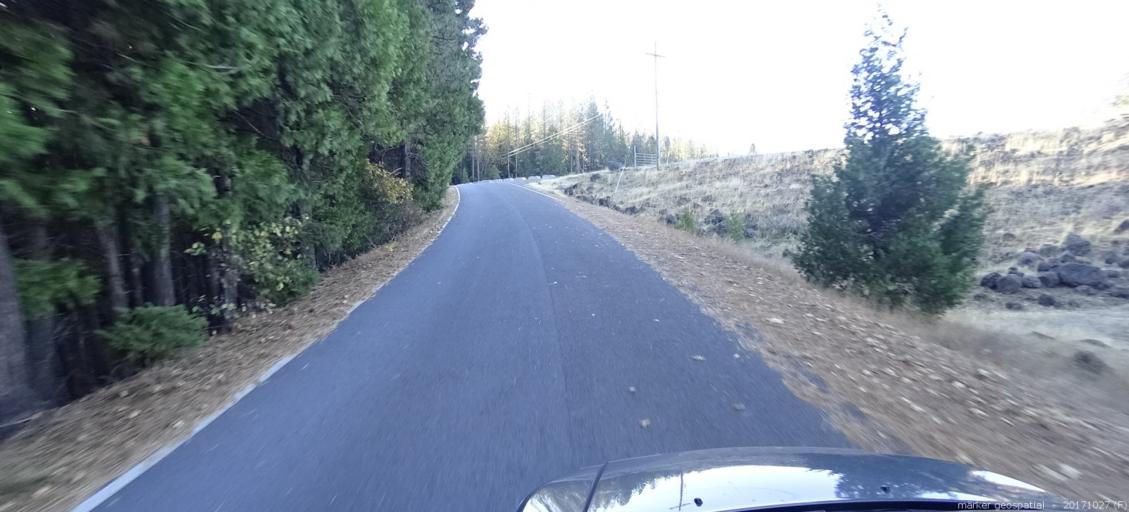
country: US
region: California
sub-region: Shasta County
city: Burney
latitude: 40.9995
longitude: -121.8862
